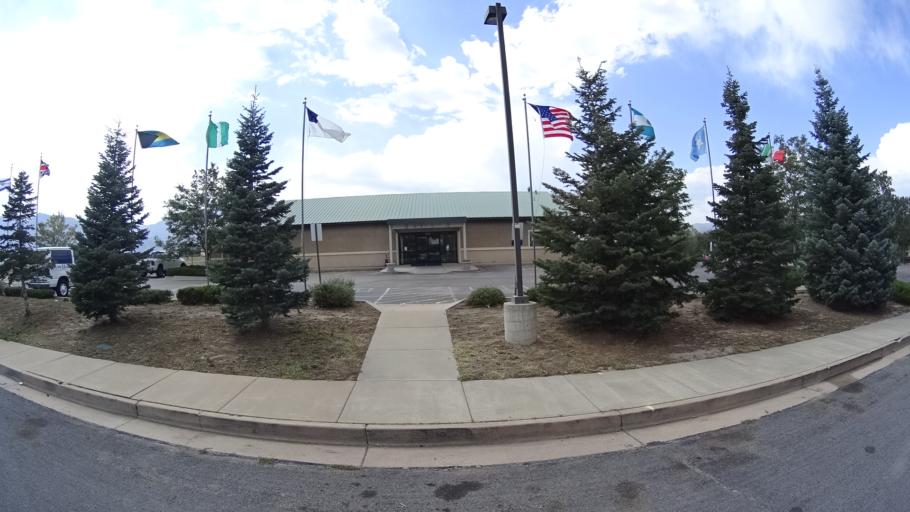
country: US
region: Colorado
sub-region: El Paso County
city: Colorado Springs
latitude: 38.8183
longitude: -104.8084
